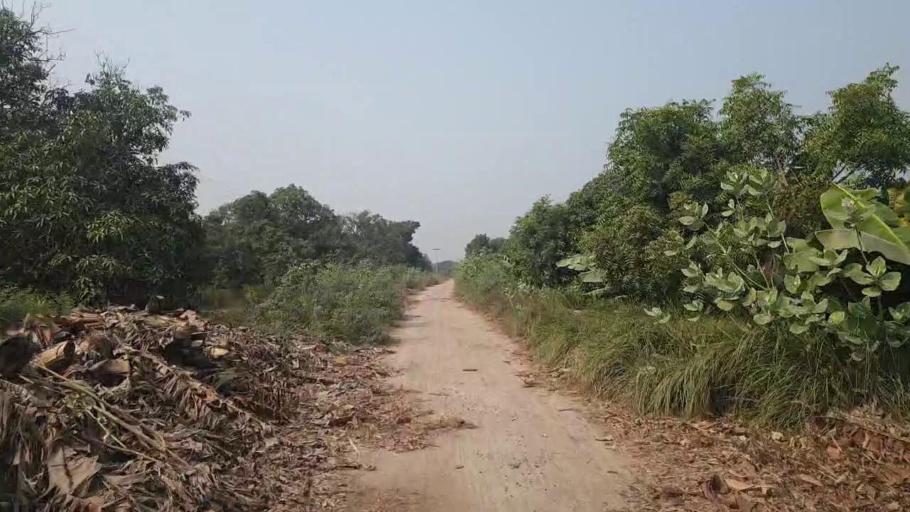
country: PK
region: Sindh
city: Tando Muhammad Khan
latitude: 25.2690
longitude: 68.5820
